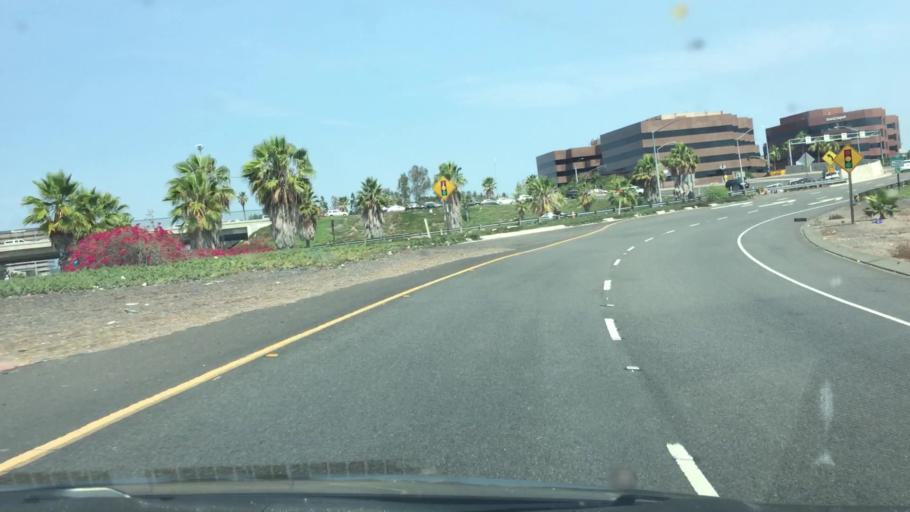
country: US
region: California
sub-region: Orange County
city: Costa Mesa
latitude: 33.6870
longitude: -117.8877
